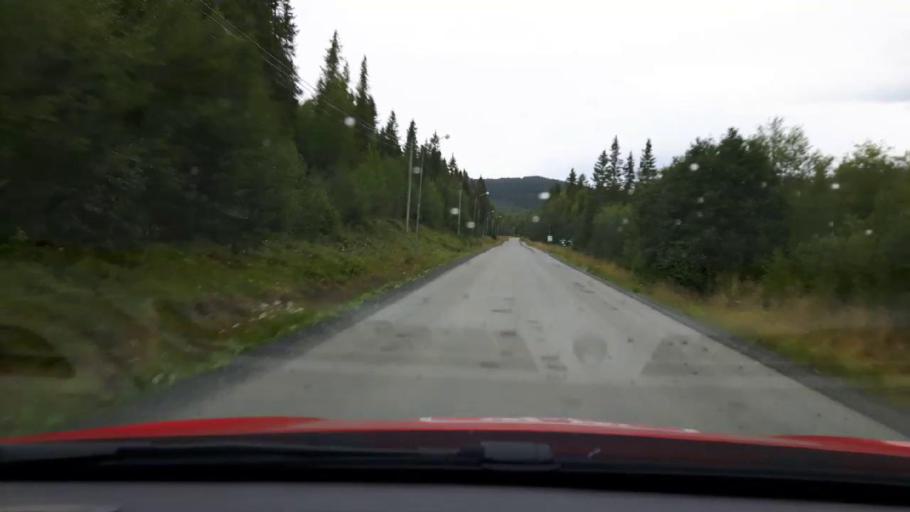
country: SE
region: Jaemtland
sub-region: Are Kommun
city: Are
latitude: 63.4859
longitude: 13.1393
